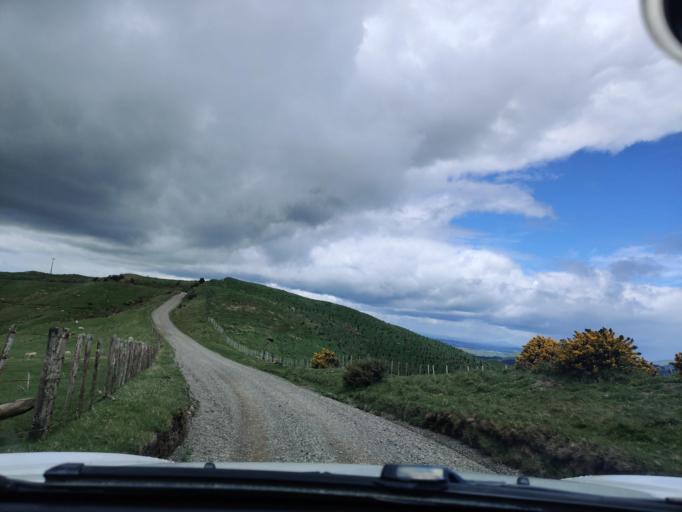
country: NZ
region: Manawatu-Wanganui
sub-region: Palmerston North City
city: Palmerston North
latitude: -40.2808
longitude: 175.8565
